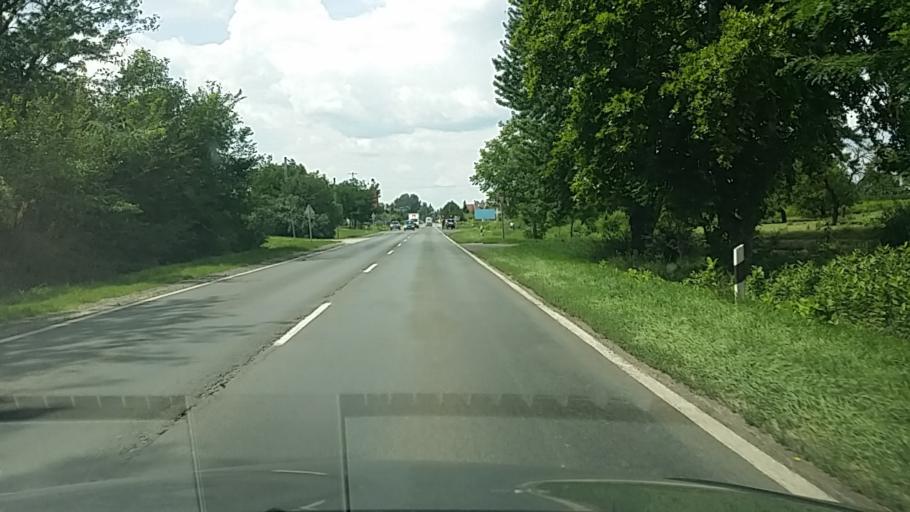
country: HU
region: Bacs-Kiskun
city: Lajosmizse
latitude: 47.0148
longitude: 19.5752
